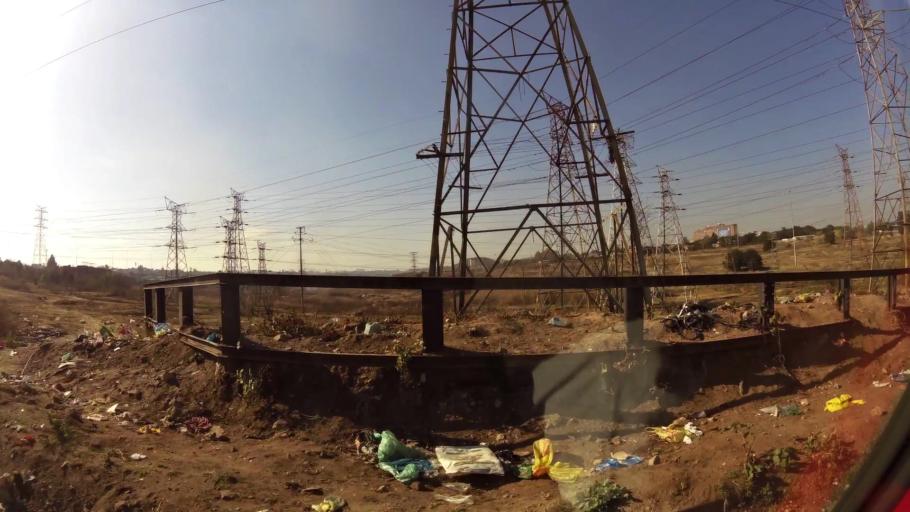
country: ZA
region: Gauteng
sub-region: City of Johannesburg Metropolitan Municipality
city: Soweto
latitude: -26.2529
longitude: 27.9320
